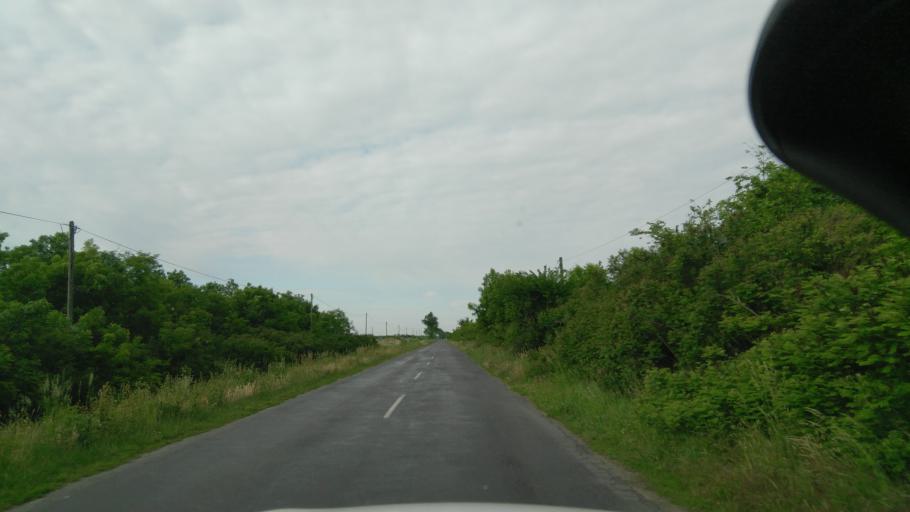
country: HU
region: Bekes
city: Elek
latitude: 46.5833
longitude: 21.2222
